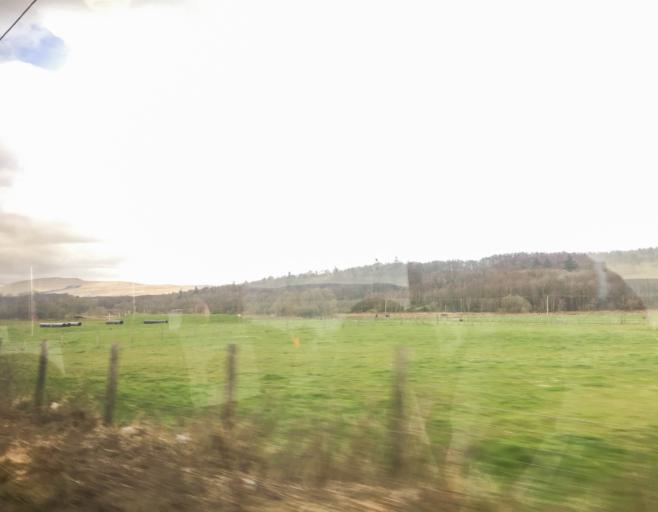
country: GB
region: Scotland
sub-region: Argyll and Bute
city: Helensburgh
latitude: 55.9860
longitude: -4.6947
